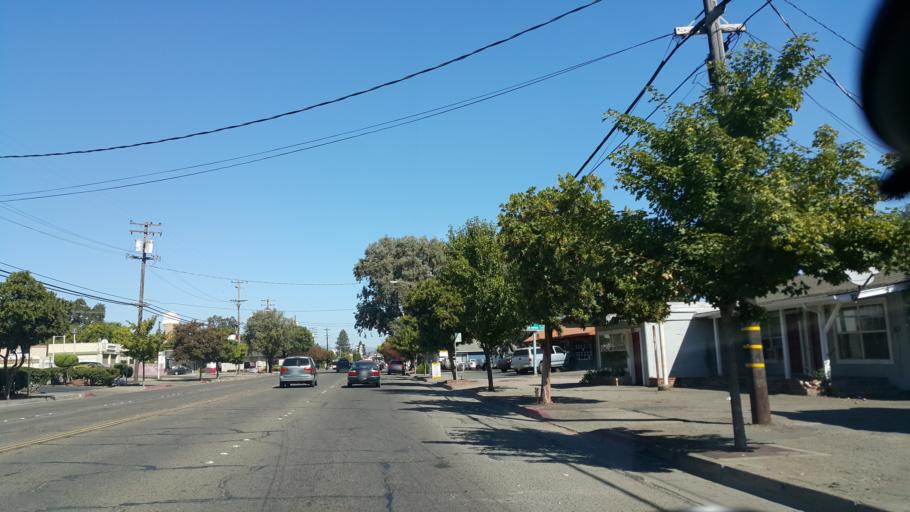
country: US
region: California
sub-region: Mendocino County
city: Ukiah
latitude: 39.1401
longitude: -123.2059
